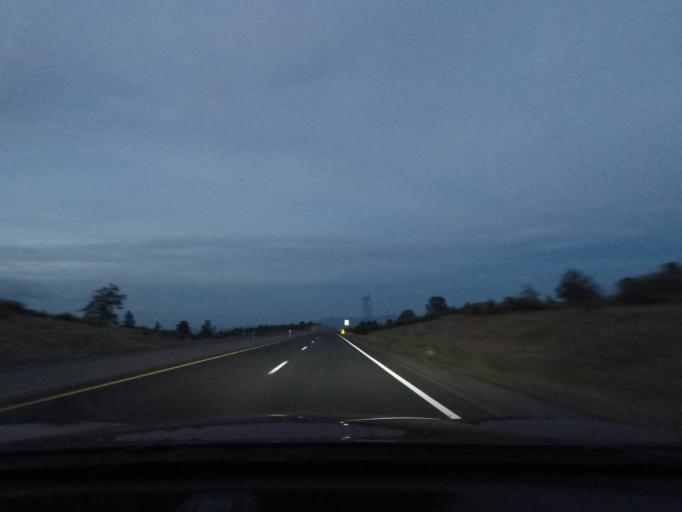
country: US
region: Arizona
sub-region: Yavapai County
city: Prescott
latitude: 34.6151
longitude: -112.4745
